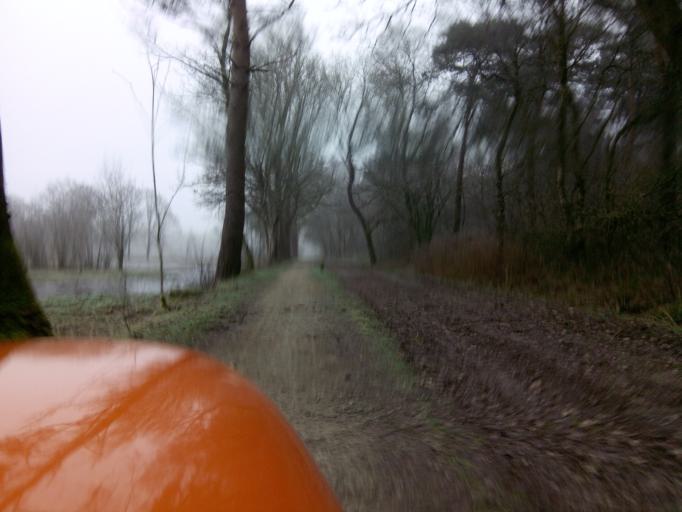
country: NL
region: Gelderland
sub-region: Gemeente Barneveld
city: Voorthuizen
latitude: 52.1954
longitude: 5.5730
